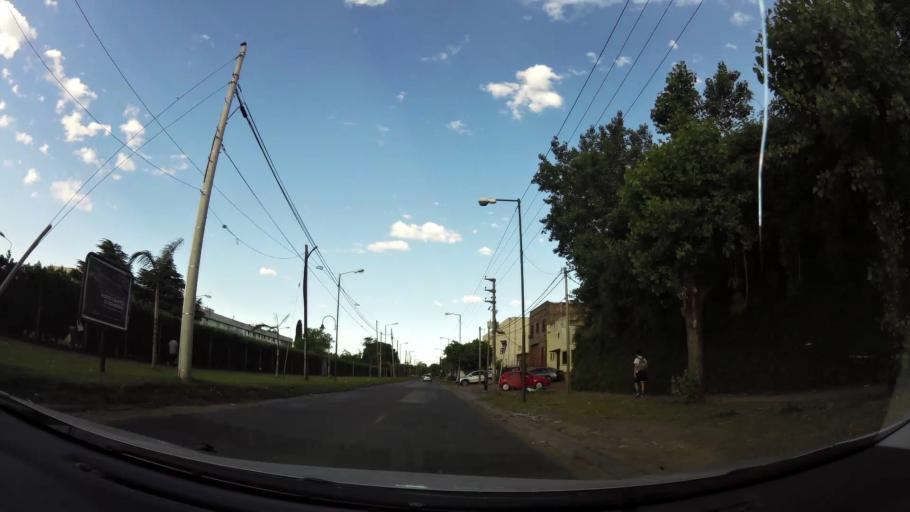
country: AR
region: Buenos Aires
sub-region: Partido de Tigre
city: Tigre
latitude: -34.4704
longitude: -58.5644
